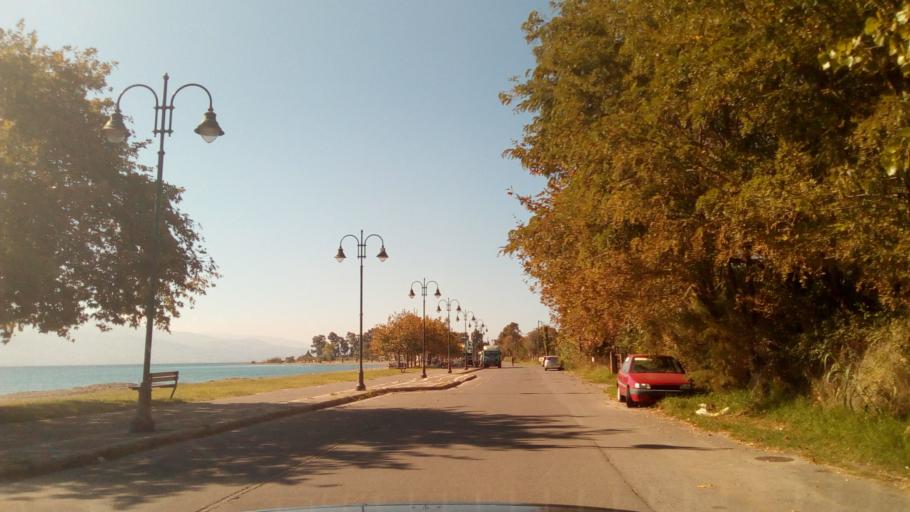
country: GR
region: West Greece
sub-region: Nomos Aitolias kai Akarnanias
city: Nafpaktos
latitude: 38.3869
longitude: 21.8207
